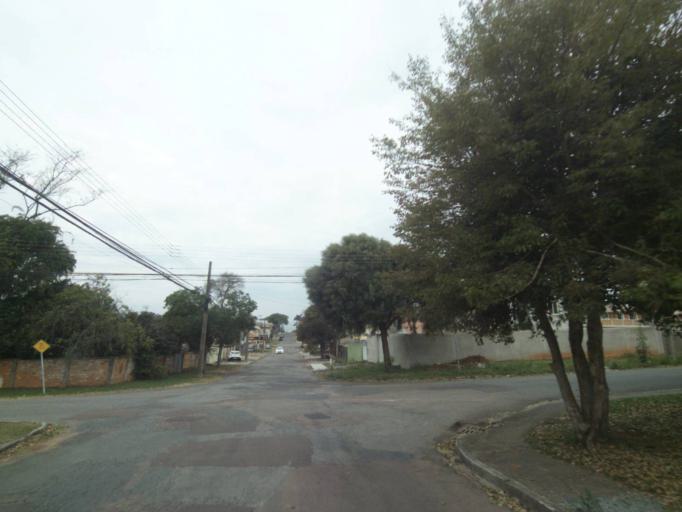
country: BR
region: Parana
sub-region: Pinhais
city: Pinhais
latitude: -25.4693
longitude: -49.2333
